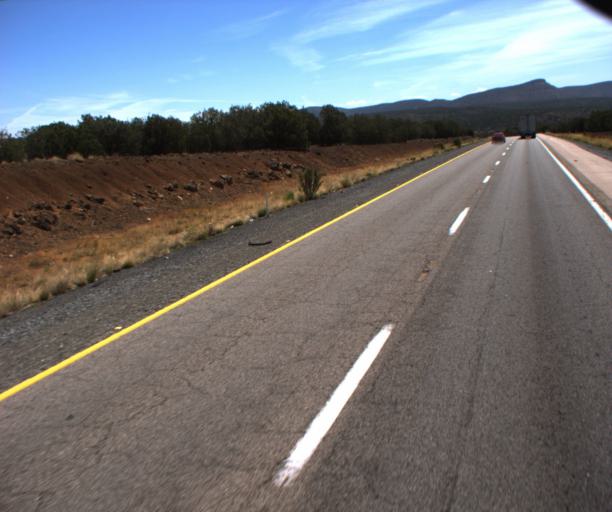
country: US
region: Arizona
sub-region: Mohave County
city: Peach Springs
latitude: 35.1898
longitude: -113.3274
